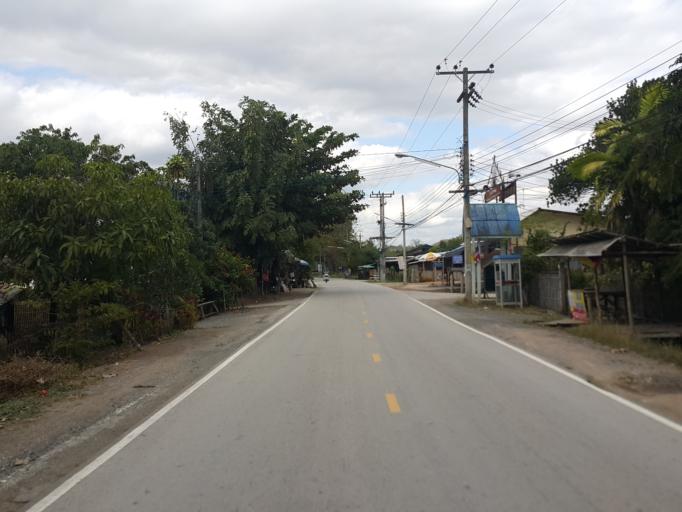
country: TH
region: Chiang Mai
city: San Sai
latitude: 18.8442
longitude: 99.1477
